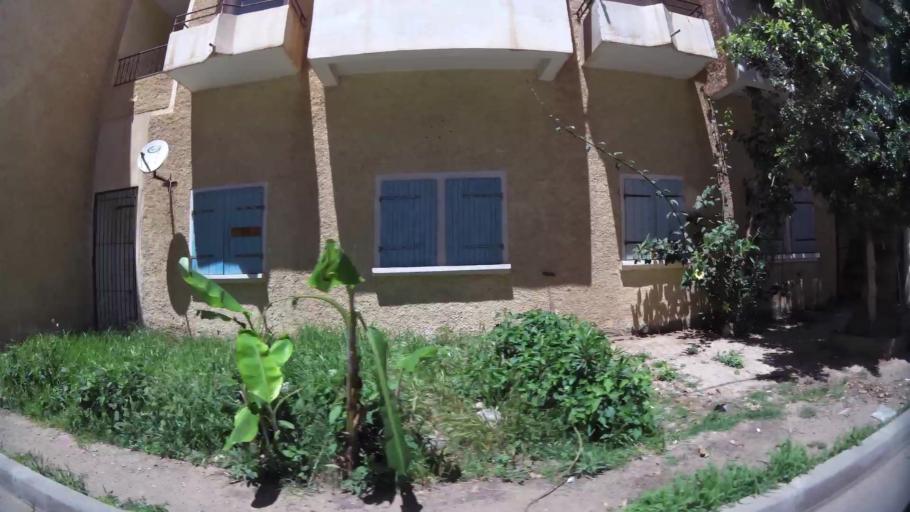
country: MA
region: Oriental
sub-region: Berkane-Taourirt
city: Madagh
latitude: 35.0772
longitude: -2.2267
